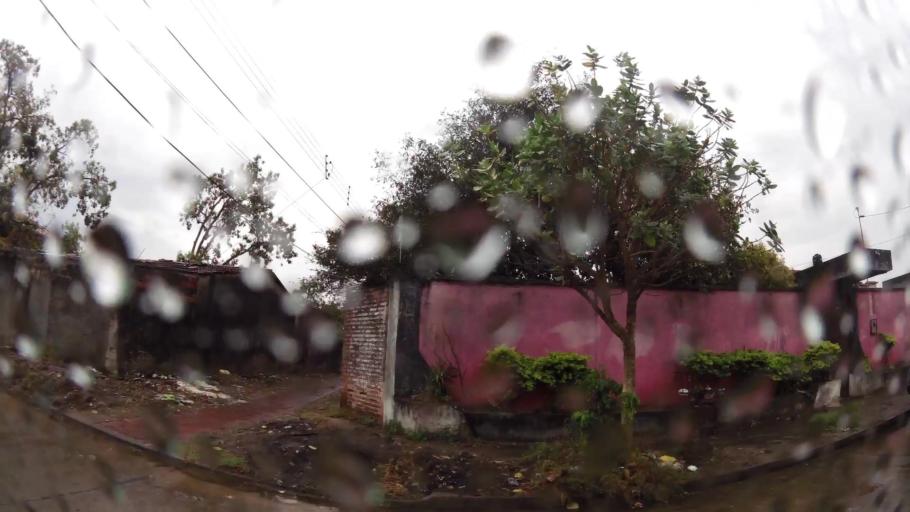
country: BO
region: Santa Cruz
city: Santa Cruz de la Sierra
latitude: -17.7950
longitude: -63.2107
